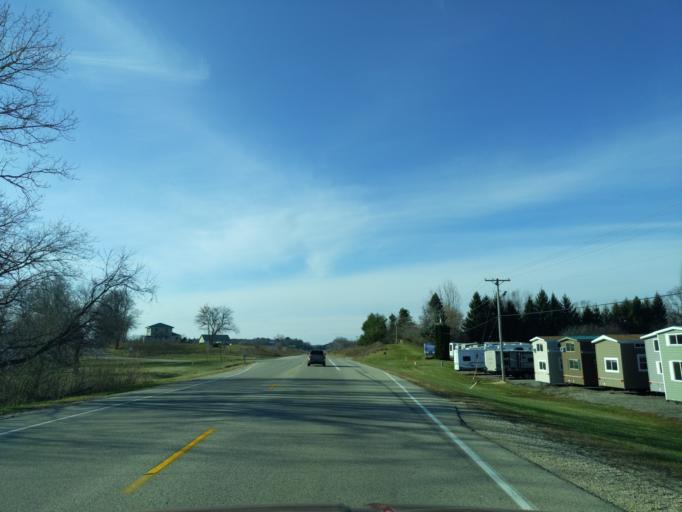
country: US
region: Wisconsin
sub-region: Rock County
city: Milton
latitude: 42.8252
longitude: -88.9864
